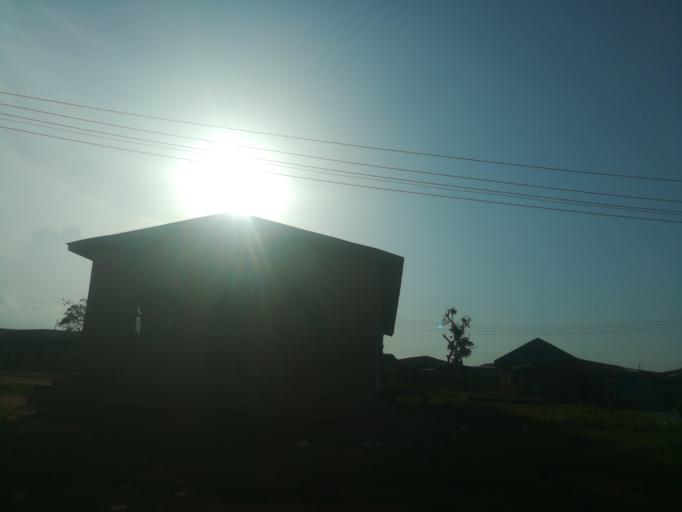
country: NG
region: Oyo
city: Moniya
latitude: 7.5678
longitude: 3.8859
